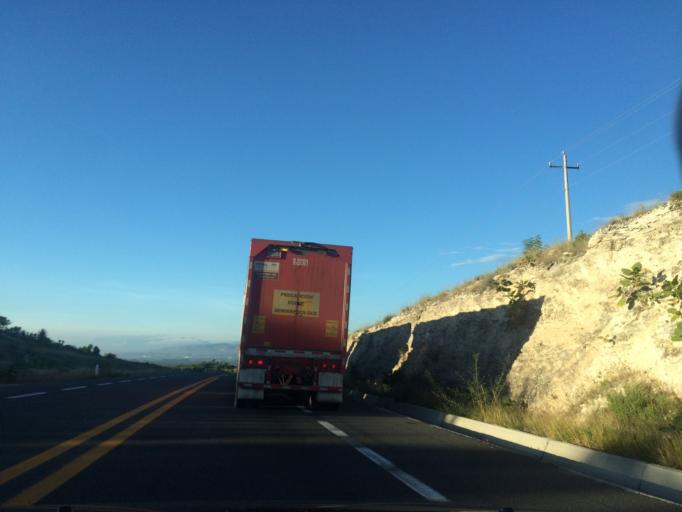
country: MX
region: Puebla
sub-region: Tehuacan
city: Magdalena Cuayucatepec
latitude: 18.5765
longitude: -97.4646
